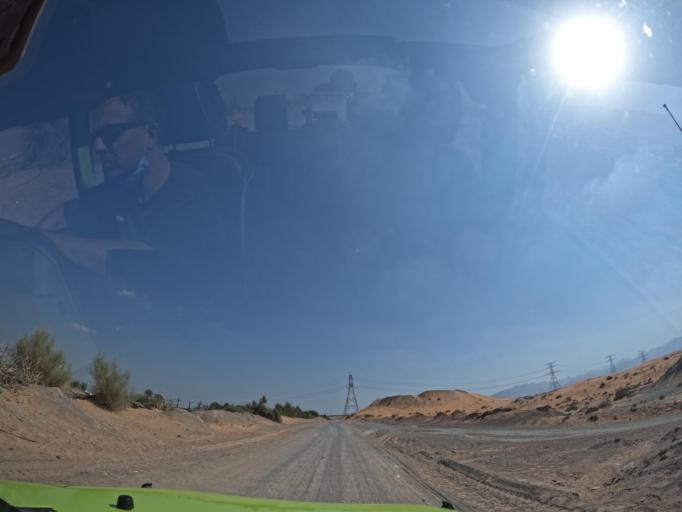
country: AE
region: Ash Shariqah
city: Adh Dhayd
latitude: 24.7995
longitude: 55.7955
